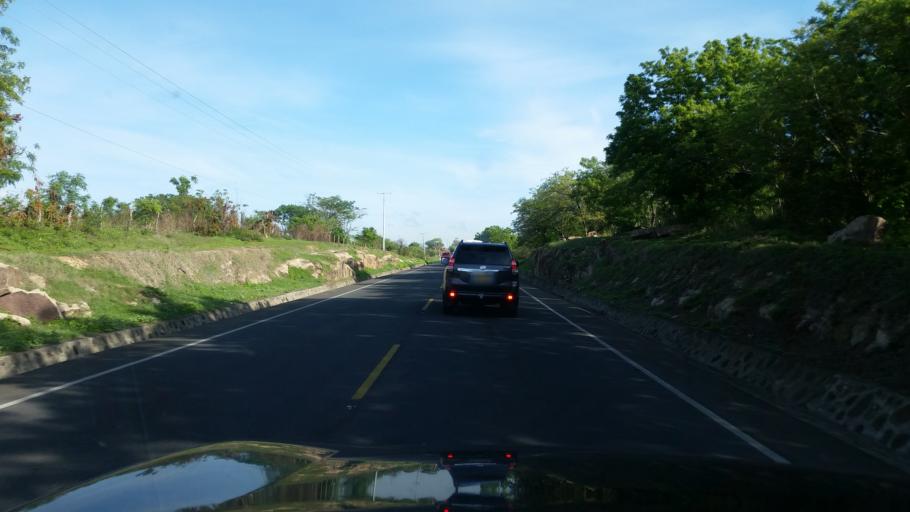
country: NI
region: Leon
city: La Paz Centro
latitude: 12.2240
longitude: -86.6960
